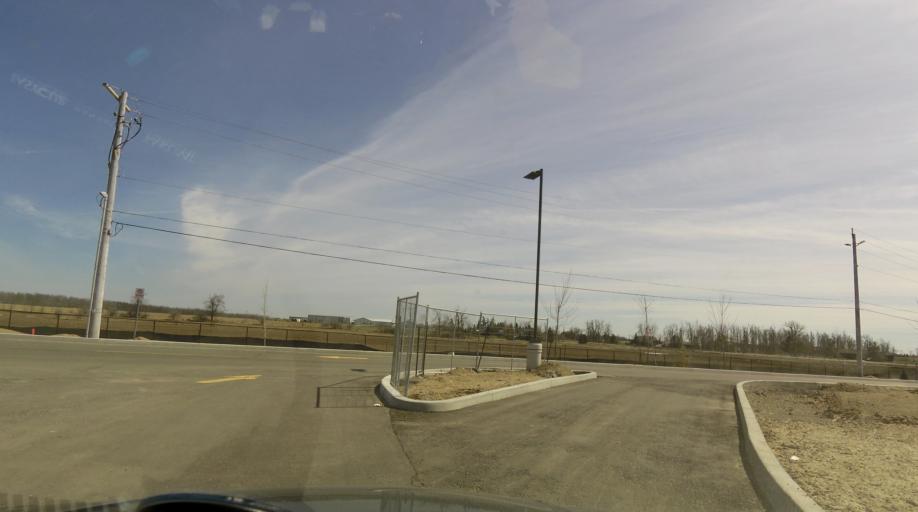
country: CA
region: Ontario
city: Brampton
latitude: 43.7017
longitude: -79.8739
